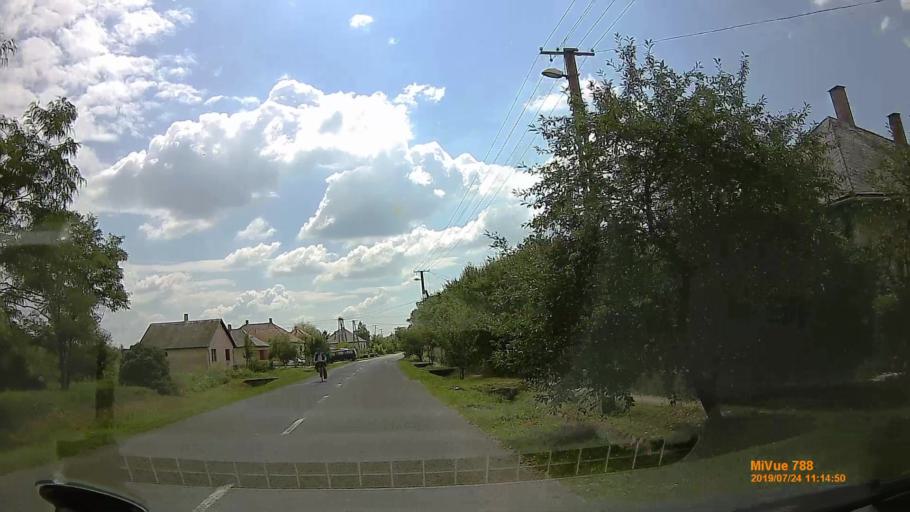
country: HU
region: Szabolcs-Szatmar-Bereg
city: Tarpa
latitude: 48.1957
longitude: 22.4521
